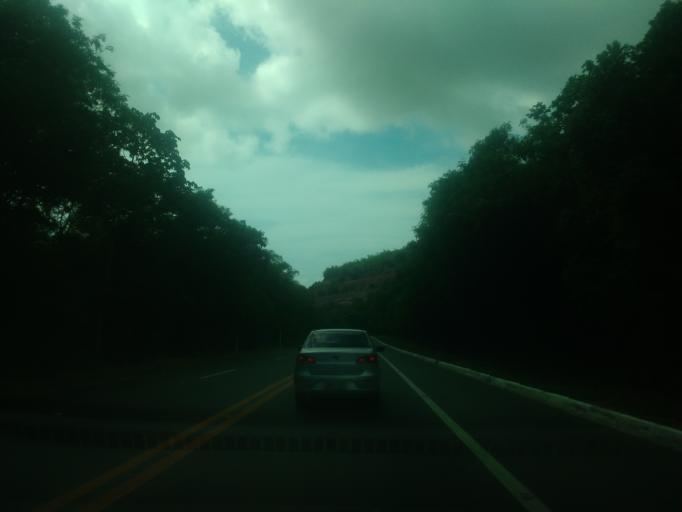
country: BR
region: Alagoas
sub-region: Marechal Deodoro
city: Marechal Deodoro
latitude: -9.6862
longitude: -35.8200
